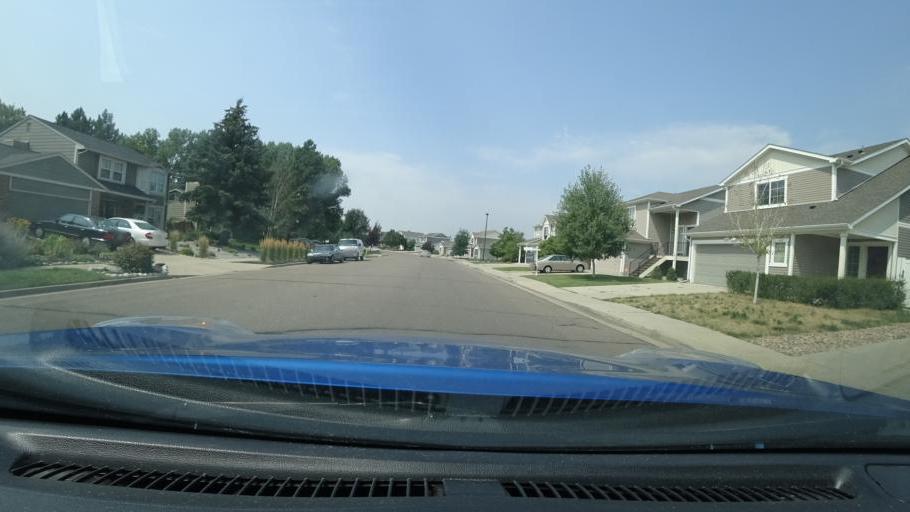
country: US
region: Colorado
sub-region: Adams County
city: Aurora
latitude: 39.7795
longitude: -104.7676
